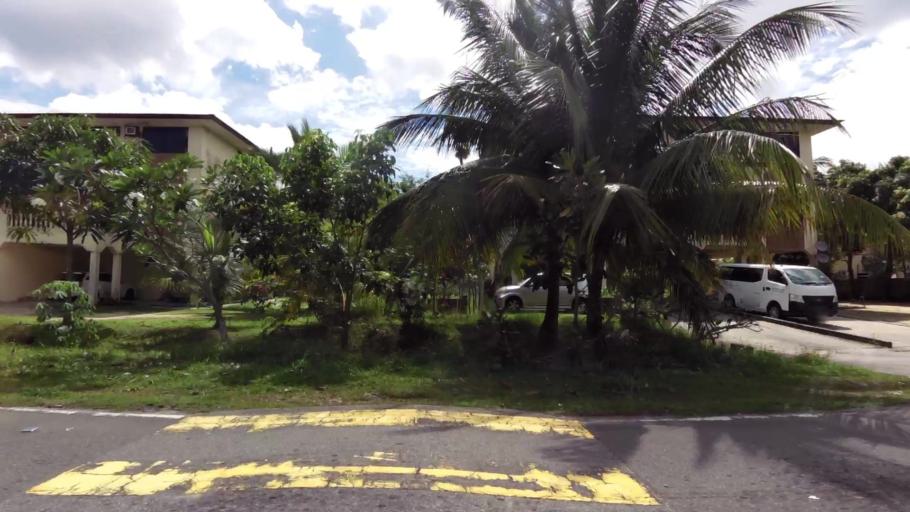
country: BN
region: Brunei and Muara
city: Bandar Seri Begawan
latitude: 4.9323
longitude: 114.8939
